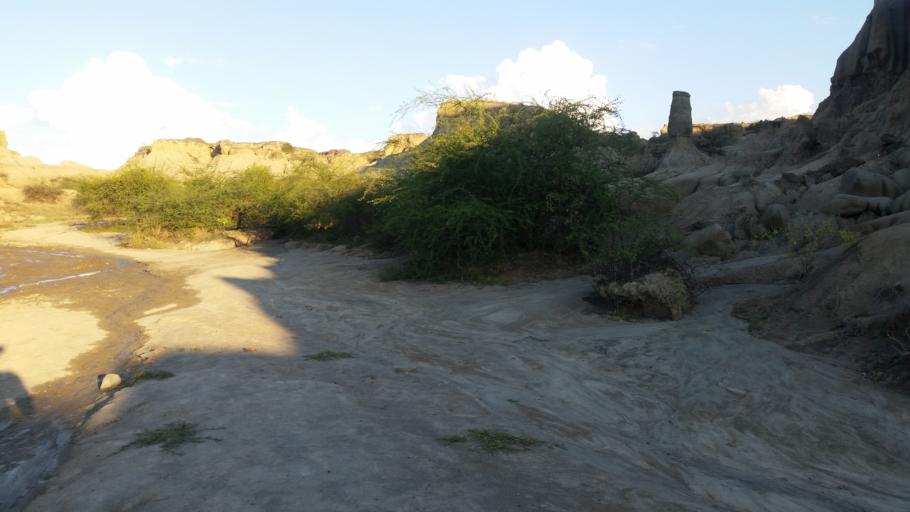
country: CO
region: Huila
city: Villavieja
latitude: 3.2394
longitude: -75.1186
